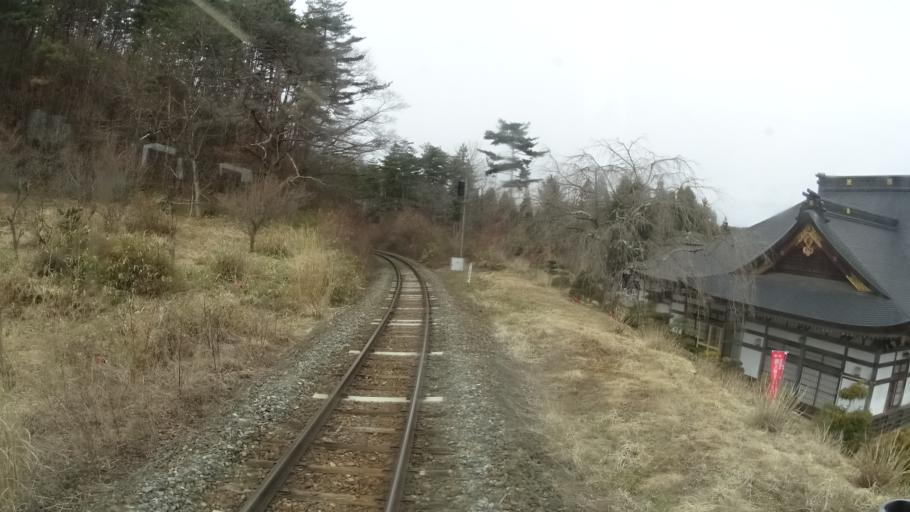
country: JP
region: Iwate
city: Tono
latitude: 39.3440
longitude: 141.3528
